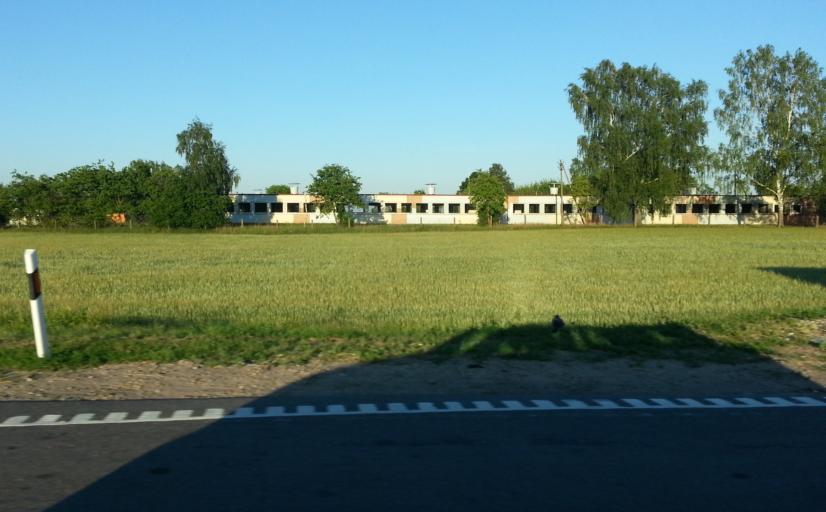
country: LT
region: Panevezys
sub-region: Panevezys City
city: Panevezys
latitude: 55.6584
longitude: 24.3596
